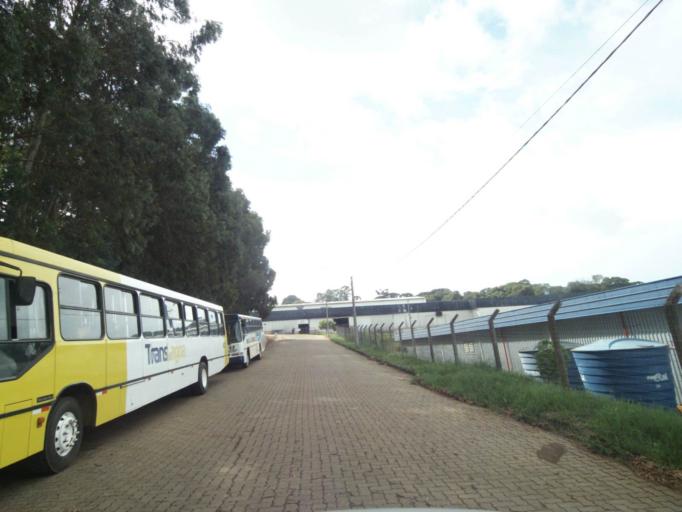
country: BR
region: Rio Grande do Sul
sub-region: Lagoa Vermelha
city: Lagoa Vermelha
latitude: -28.2268
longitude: -51.5124
